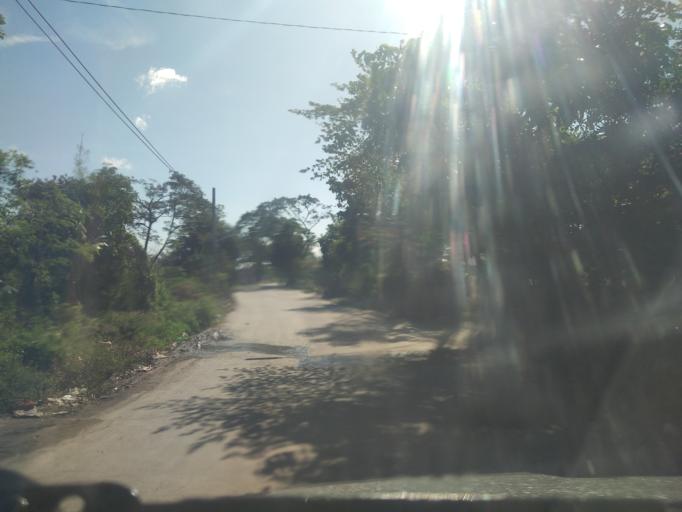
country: PH
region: Central Luzon
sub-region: Province of Pampanga
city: Calibutbut
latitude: 15.0874
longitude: 120.6028
